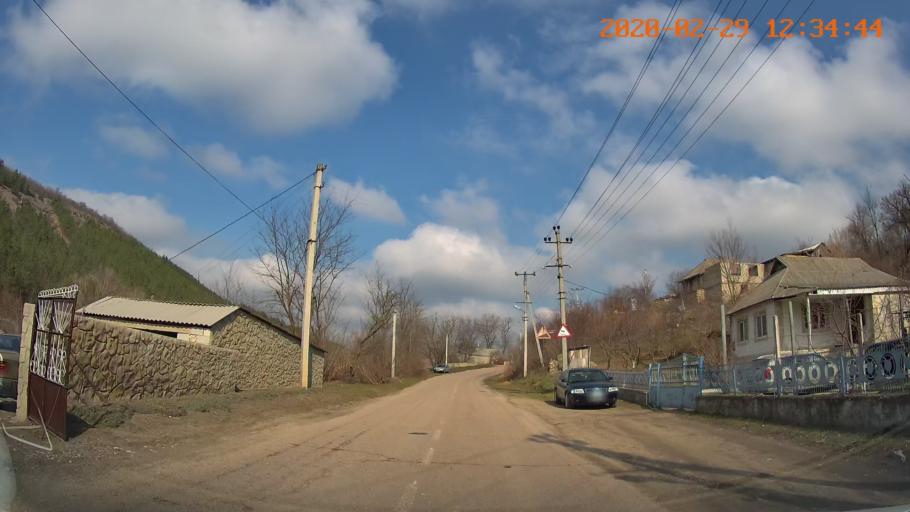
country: MD
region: Telenesti
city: Camenca
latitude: 48.0420
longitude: 28.7160
